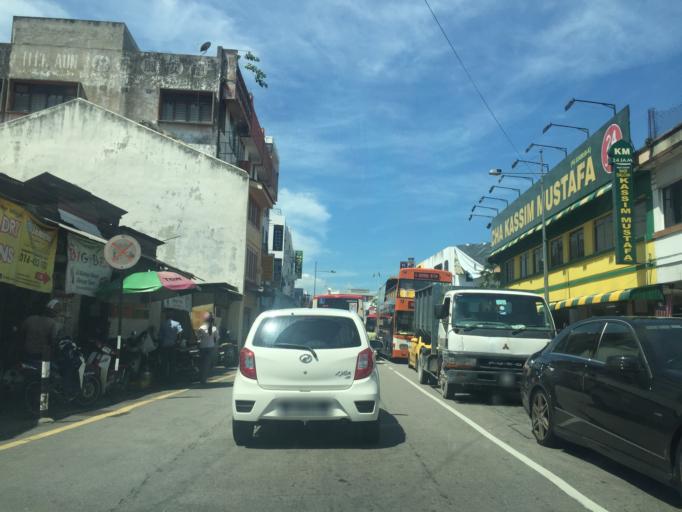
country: MY
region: Penang
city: George Town
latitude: 5.4154
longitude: 100.3395
